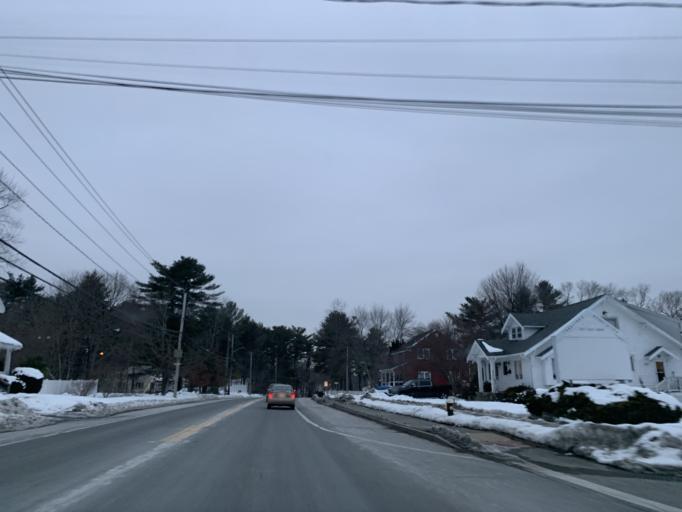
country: US
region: Massachusetts
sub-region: Norfolk County
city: Stoughton
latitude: 42.1147
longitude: -71.0799
